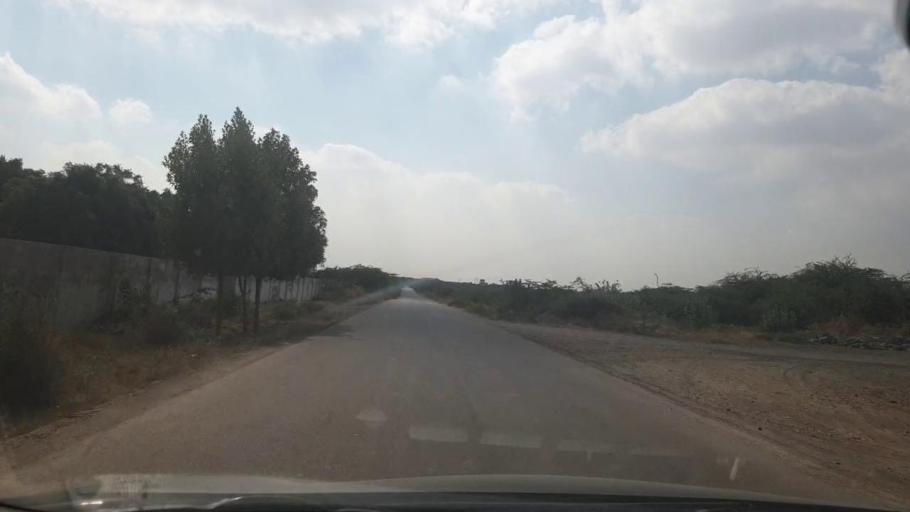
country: PK
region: Sindh
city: Malir Cantonment
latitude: 25.0200
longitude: 67.3545
